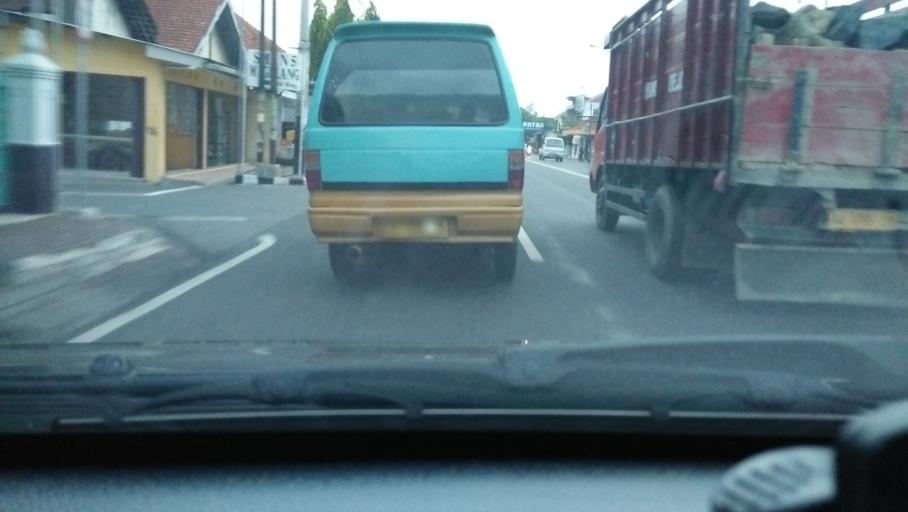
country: ID
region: Central Java
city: Magelang
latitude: -7.4477
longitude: 110.2249
